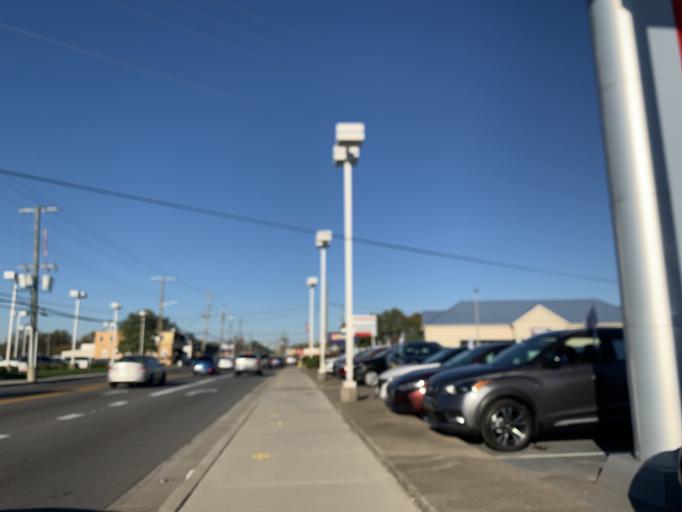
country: US
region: Kentucky
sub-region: Jefferson County
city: Shively
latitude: 38.1904
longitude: -85.8092
